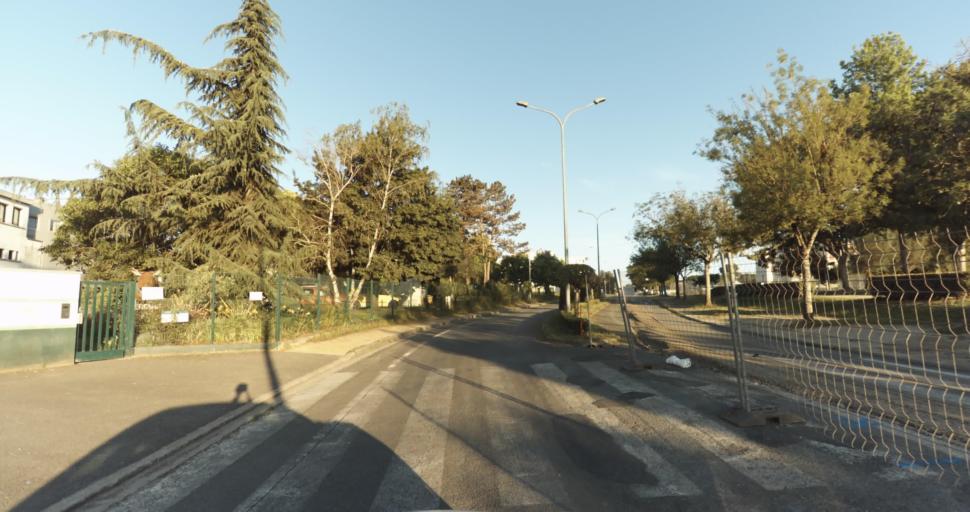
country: FR
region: Aquitaine
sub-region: Departement de la Gironde
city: Bazas
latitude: 44.4326
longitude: -0.2209
